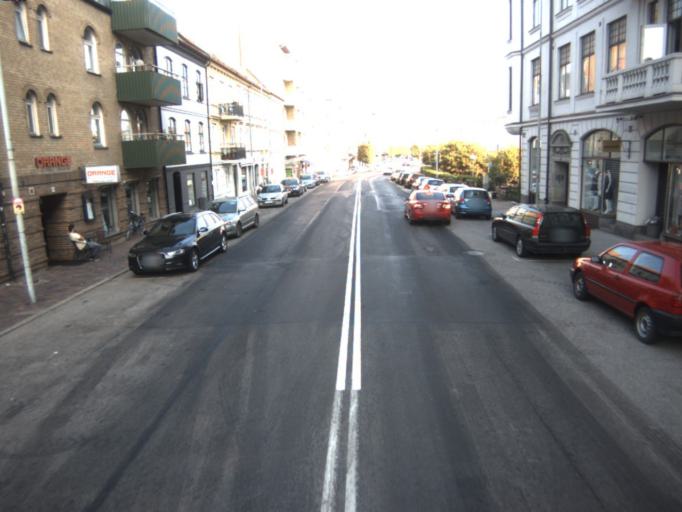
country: SE
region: Skane
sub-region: Helsingborg
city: Helsingborg
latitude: 56.0517
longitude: 12.6877
